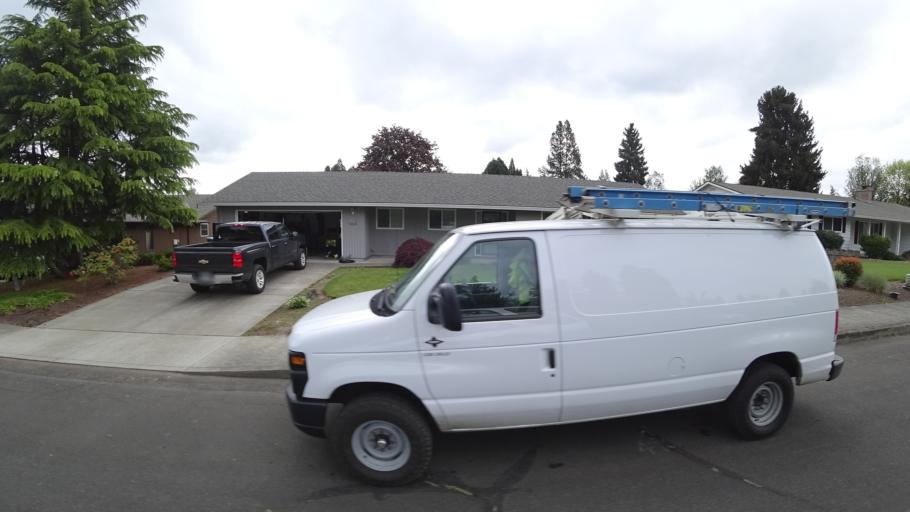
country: US
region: Oregon
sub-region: Washington County
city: Hillsboro
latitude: 45.5316
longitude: -122.9832
